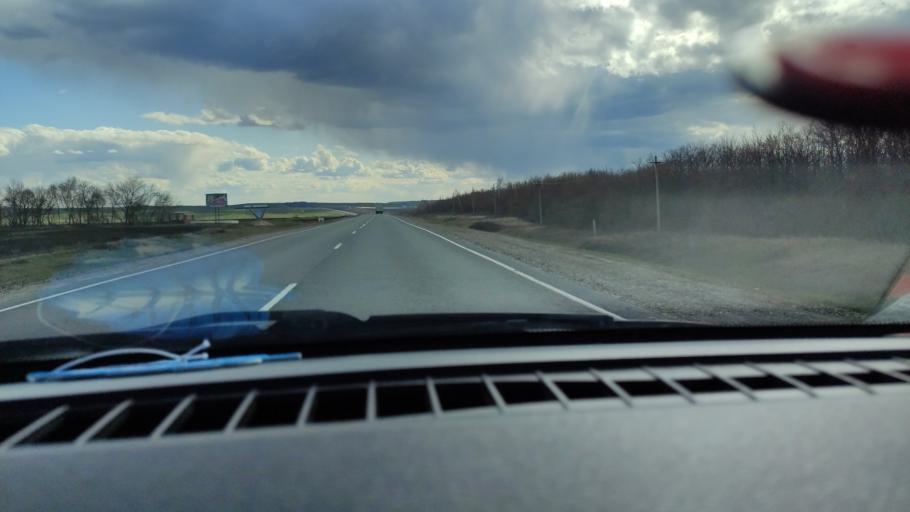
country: RU
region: Saratov
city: Alekseyevka
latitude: 52.2622
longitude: 47.9219
